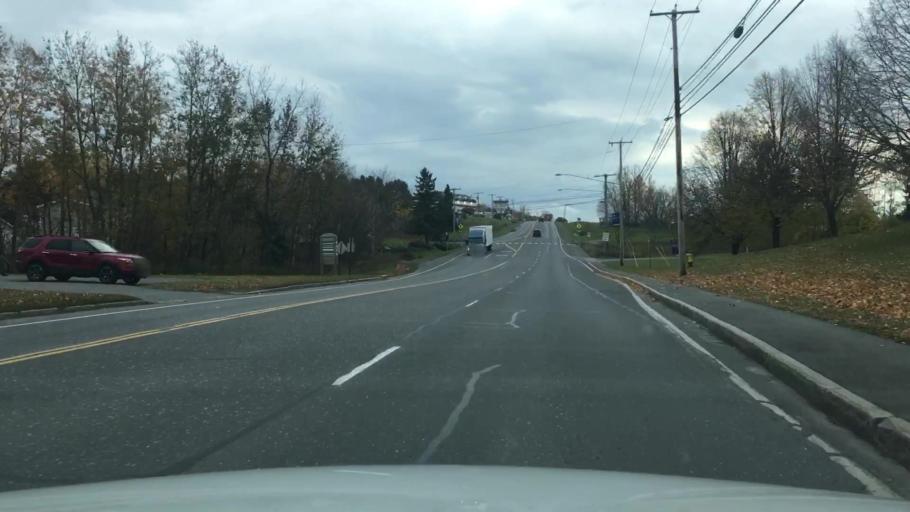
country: US
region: Maine
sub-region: Aroostook County
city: Presque Isle
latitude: 46.6713
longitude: -68.0144
